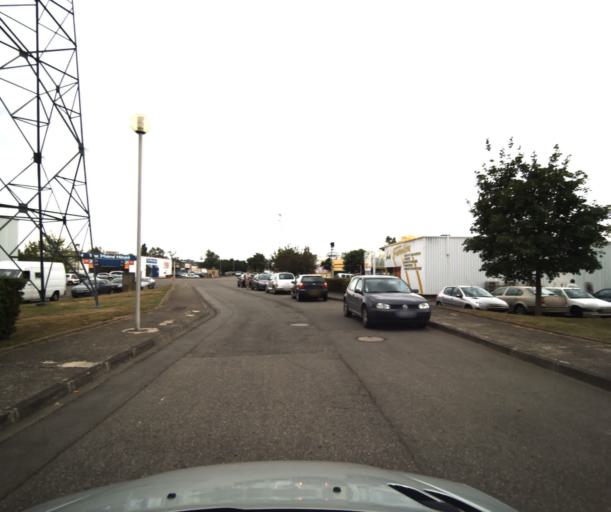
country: FR
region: Midi-Pyrenees
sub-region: Departement de la Haute-Garonne
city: Portet-sur-Garonne
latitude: 43.5330
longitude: 1.3969
